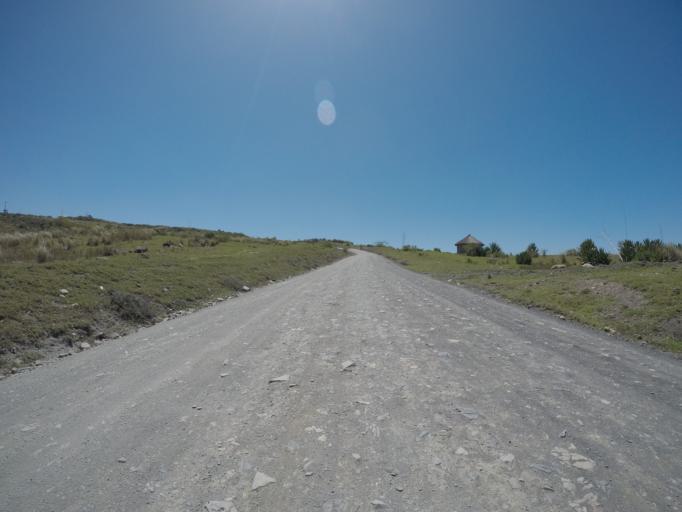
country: ZA
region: Eastern Cape
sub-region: OR Tambo District Municipality
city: Libode
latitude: -31.9781
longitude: 29.0352
